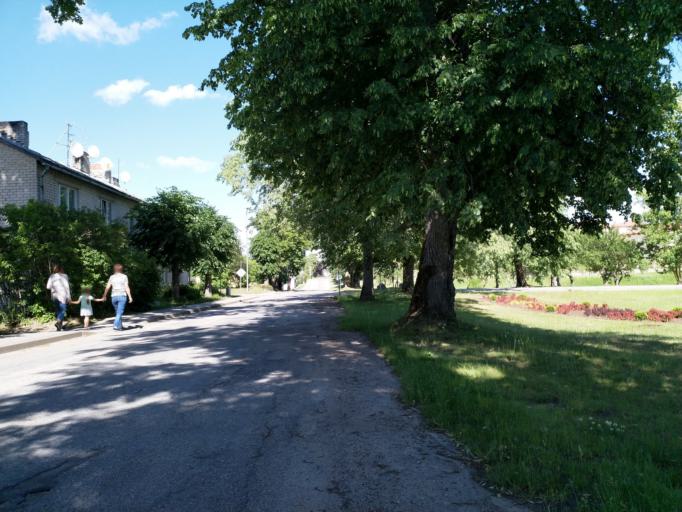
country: LV
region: Alsunga
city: Alsunga
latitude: 56.9784
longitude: 21.5649
